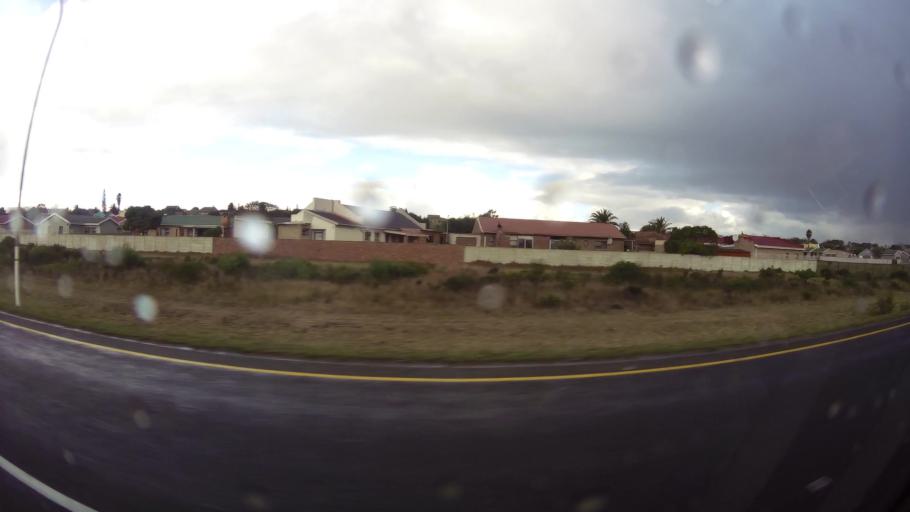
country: ZA
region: Western Cape
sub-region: Eden District Municipality
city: Mossel Bay
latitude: -34.1832
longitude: 22.1071
